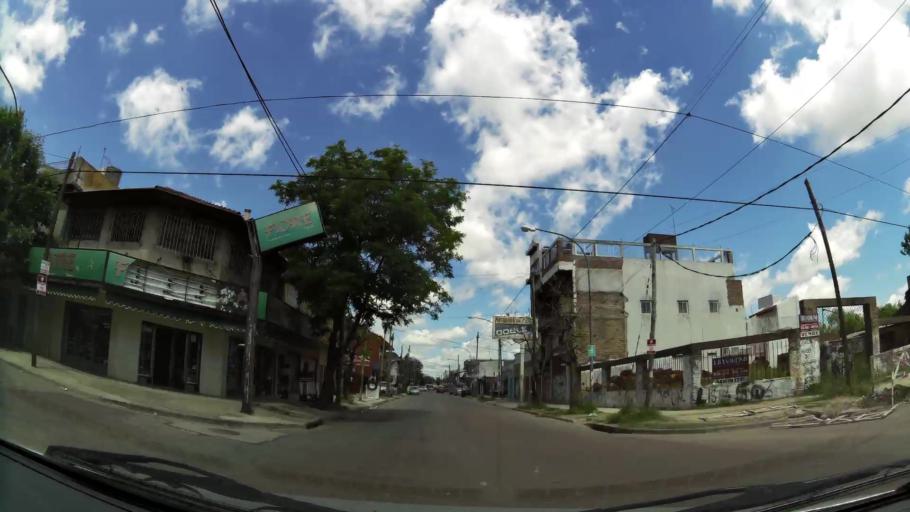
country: AR
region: Buenos Aires
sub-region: Partido de Lanus
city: Lanus
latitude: -34.6975
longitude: -58.4269
